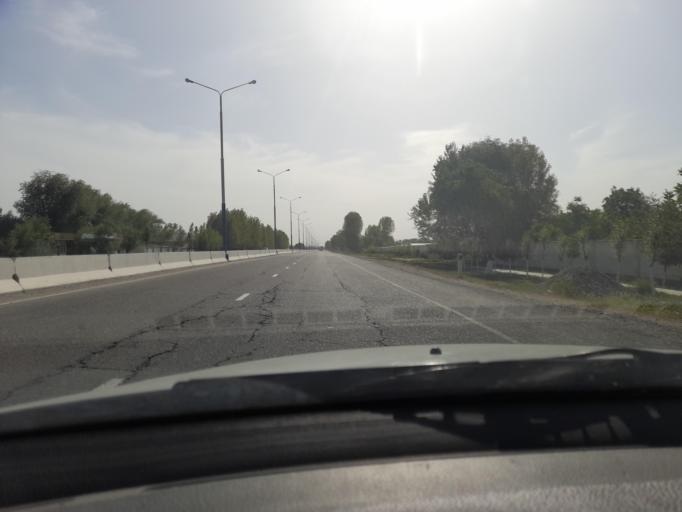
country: UZ
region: Samarqand
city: Ishtixon
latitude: 39.9391
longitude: 66.3886
